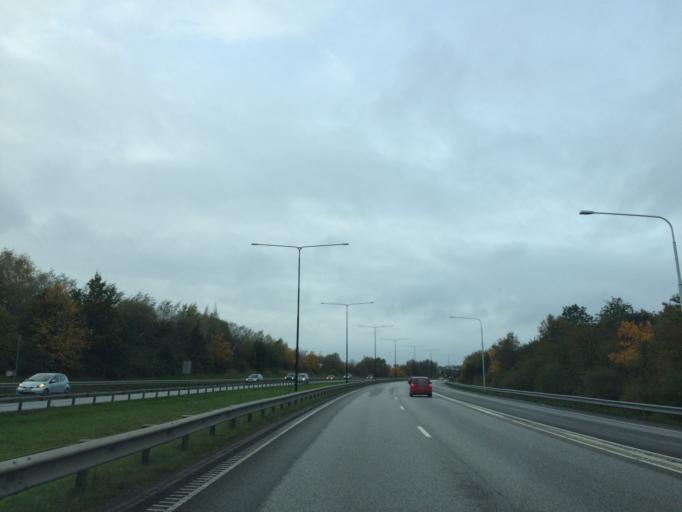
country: SE
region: Skane
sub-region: Malmo
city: Malmoe
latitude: 55.5677
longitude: 13.0420
